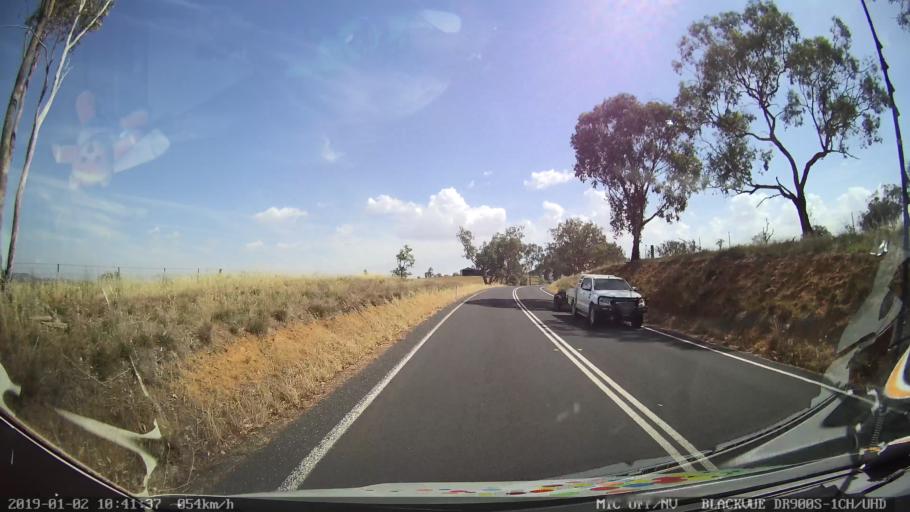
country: AU
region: New South Wales
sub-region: Cootamundra
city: Cootamundra
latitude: -34.7926
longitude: 148.3066
